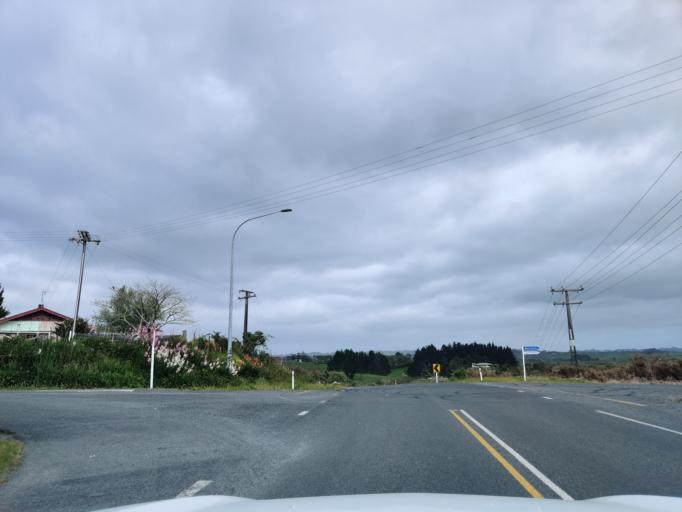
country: NZ
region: Waikato
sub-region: Waikato District
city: Ngaruawahia
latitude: -37.5777
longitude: 175.1343
